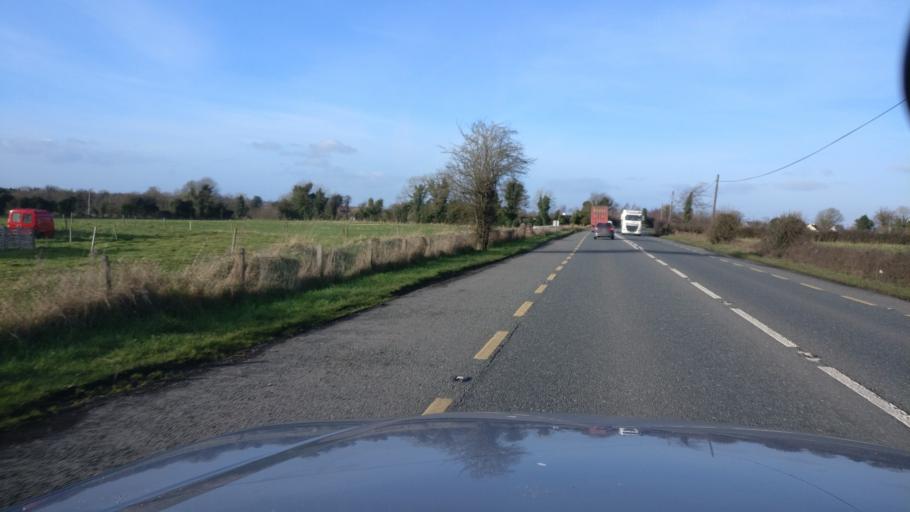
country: IE
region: Leinster
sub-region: Uibh Fhaili
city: Tullamore
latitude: 53.2351
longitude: -7.4777
